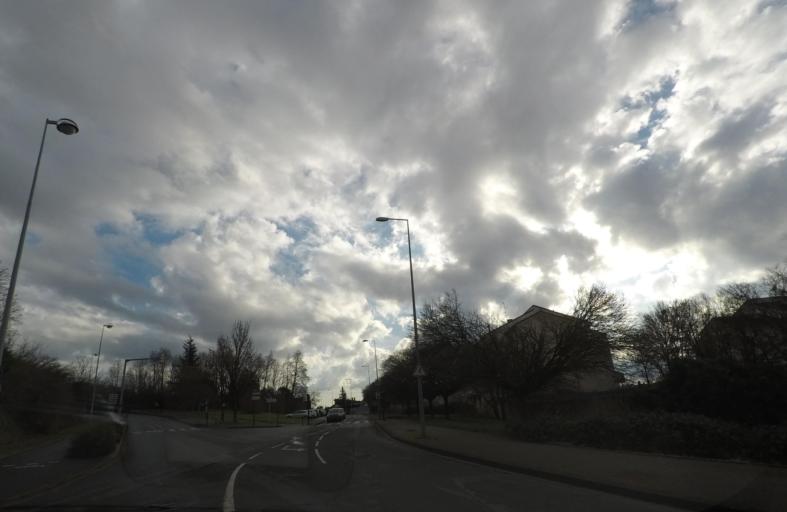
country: FR
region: Centre
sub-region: Departement du Cher
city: Bourges
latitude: 47.0606
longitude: 2.4013
